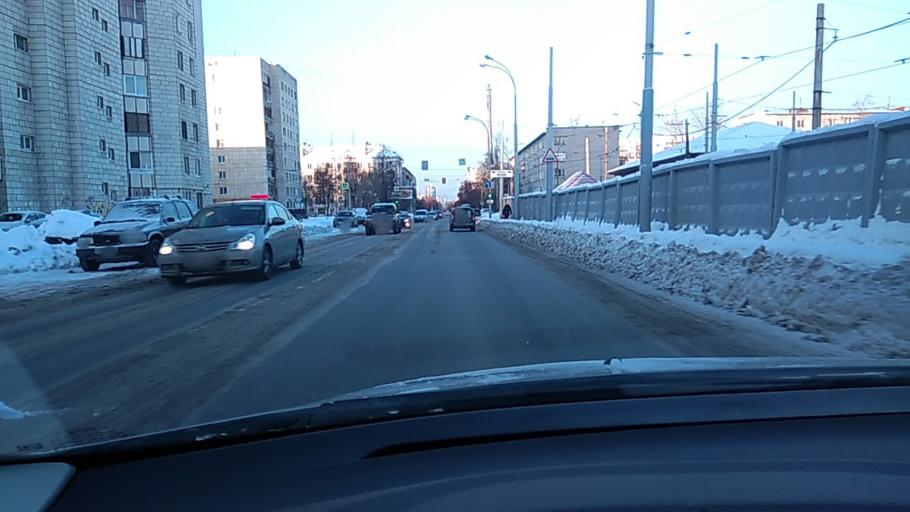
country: RU
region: Sverdlovsk
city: Yekaterinburg
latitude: 56.8126
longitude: 60.6117
